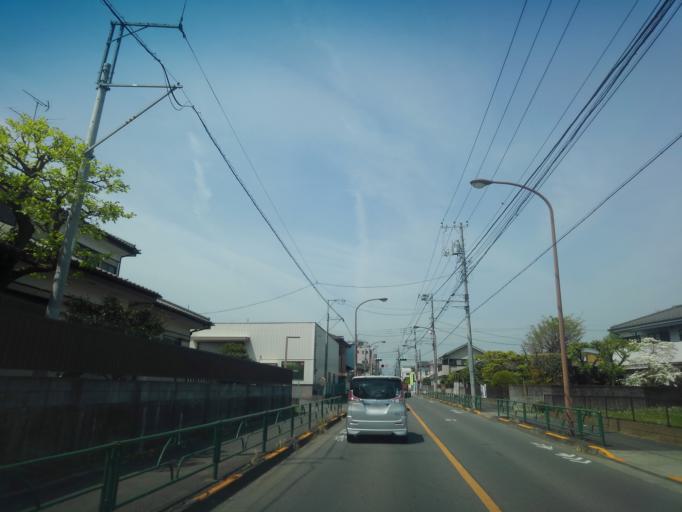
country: JP
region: Tokyo
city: Higashimurayama-shi
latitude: 35.7542
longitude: 139.3980
